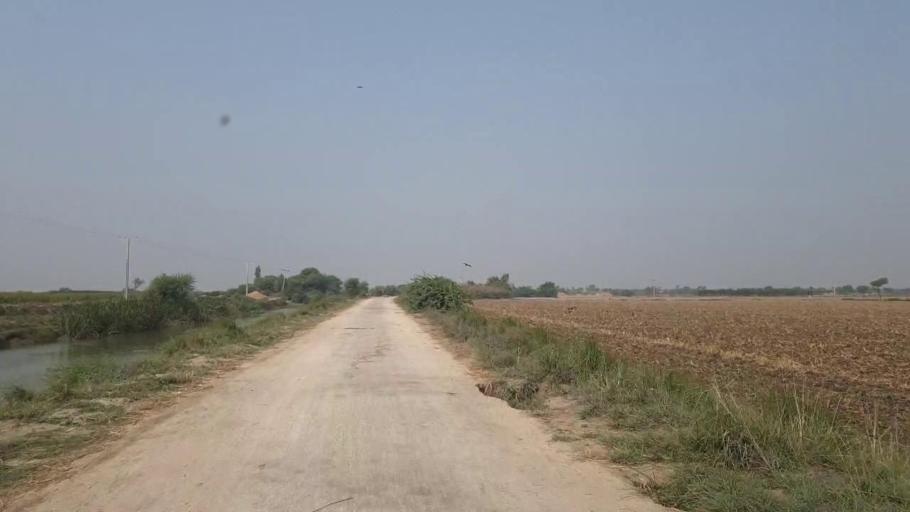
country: PK
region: Sindh
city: Kario
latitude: 24.9136
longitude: 68.6029
